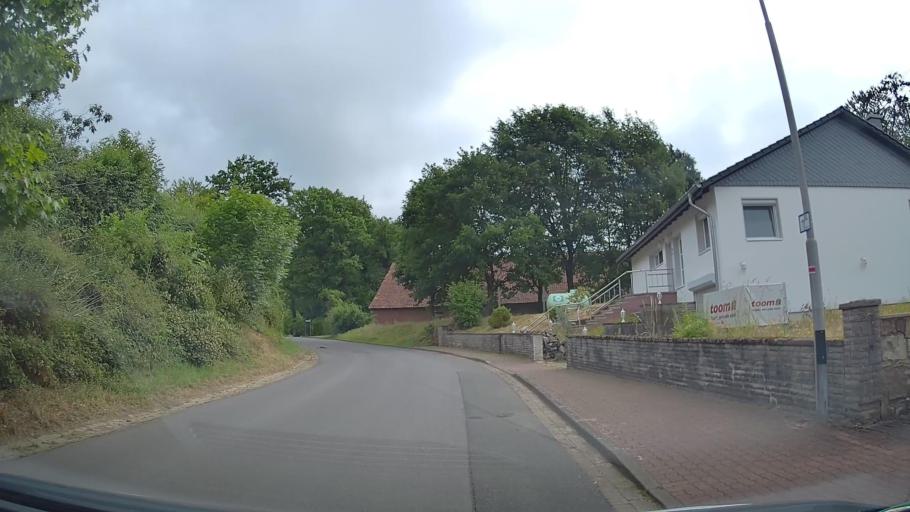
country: DE
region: Lower Saxony
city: Aerzen
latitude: 52.0434
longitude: 9.1951
